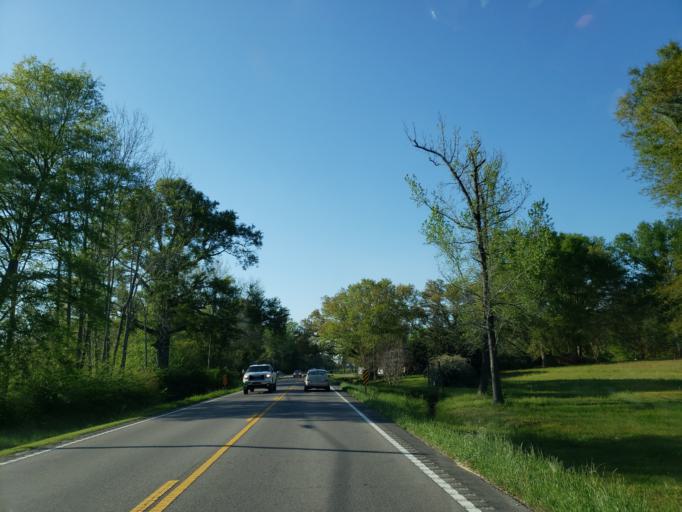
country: US
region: Mississippi
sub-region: Jones County
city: Laurel
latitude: 31.6258
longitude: -89.0893
